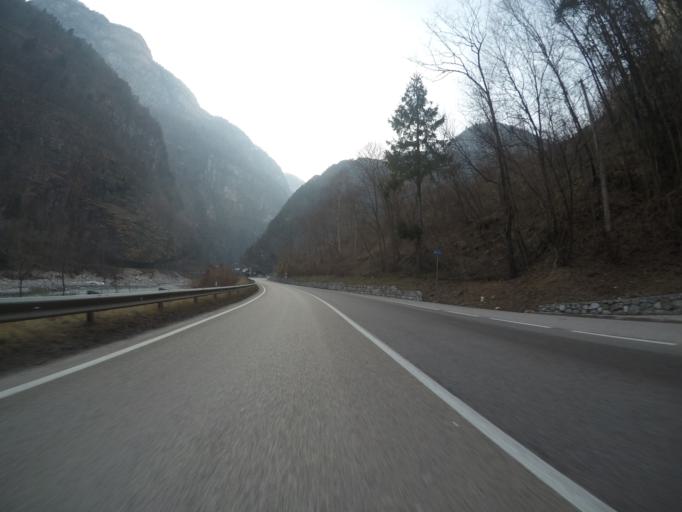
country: IT
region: Veneto
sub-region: Provincia di Belluno
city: La Valle Agordina
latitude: 46.2494
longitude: 12.0882
